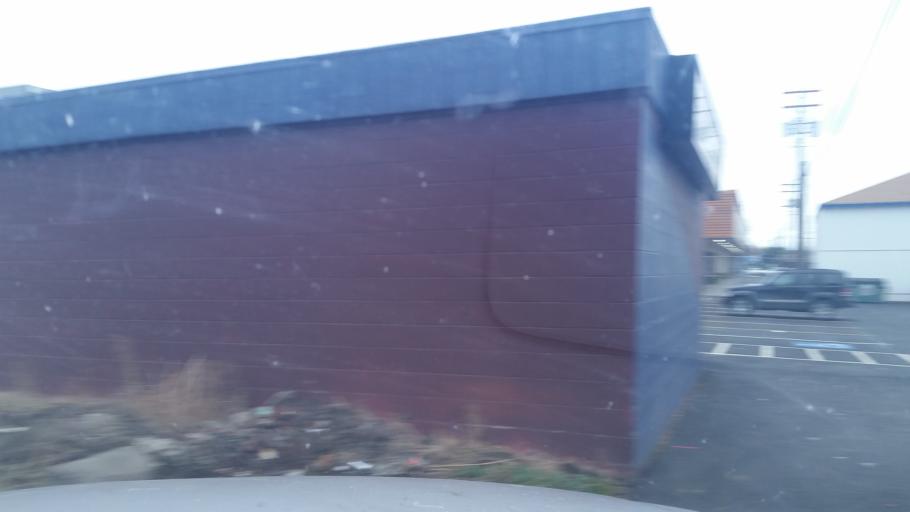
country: US
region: Washington
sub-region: Spokane County
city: Cheney
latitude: 47.4968
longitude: -117.5662
